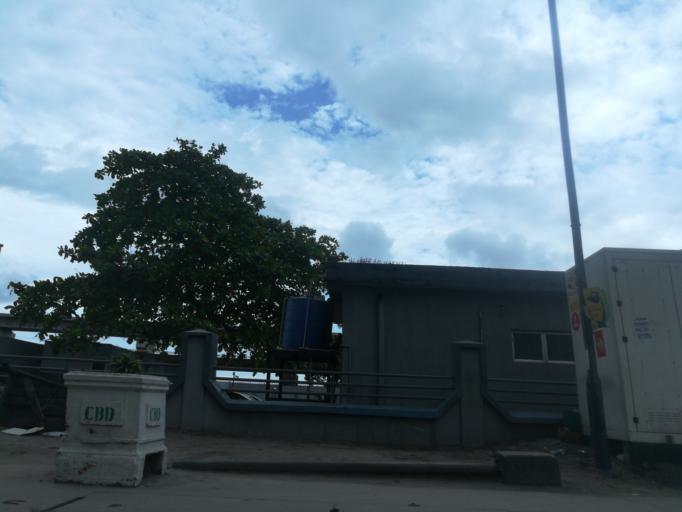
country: NG
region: Lagos
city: Lagos
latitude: 6.4528
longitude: 3.3868
